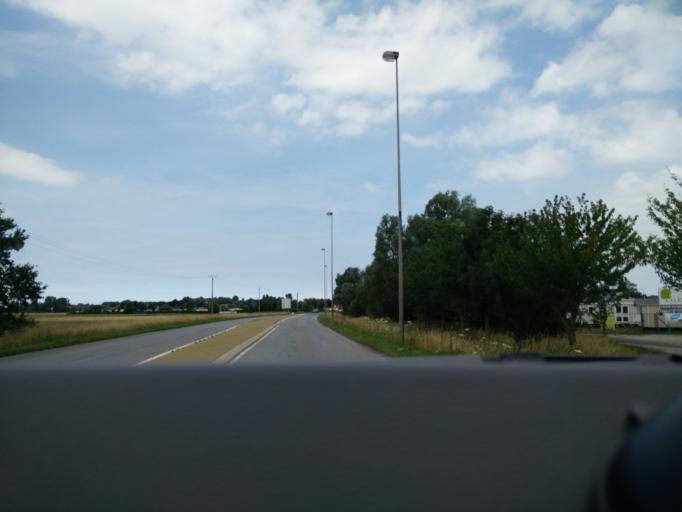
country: FR
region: Nord-Pas-de-Calais
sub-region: Departement du Nord
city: Ghyvelde
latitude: 51.0479
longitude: 2.5186
